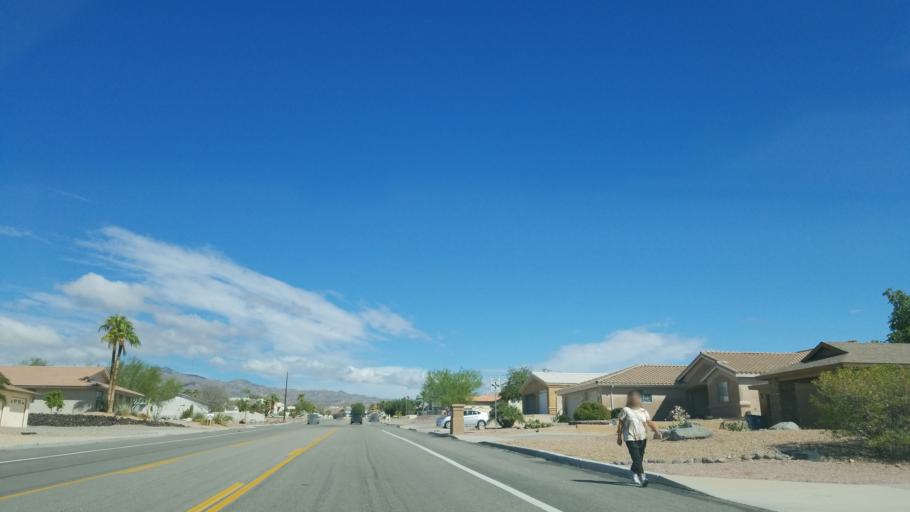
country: US
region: Arizona
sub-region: Mohave County
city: Lake Havasu City
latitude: 34.4538
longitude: -114.2641
